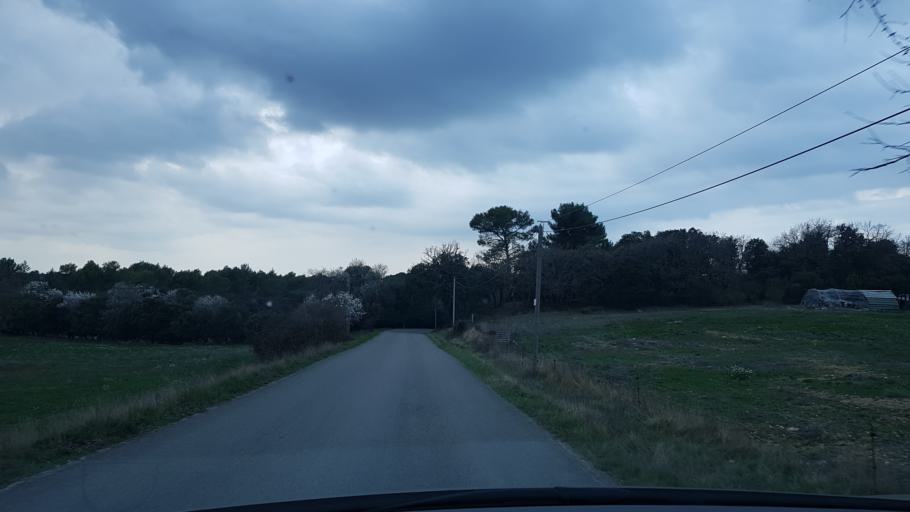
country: FR
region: Provence-Alpes-Cote d'Azur
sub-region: Departement des Bouches-du-Rhone
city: Mimet
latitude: 43.4247
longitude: 5.5143
